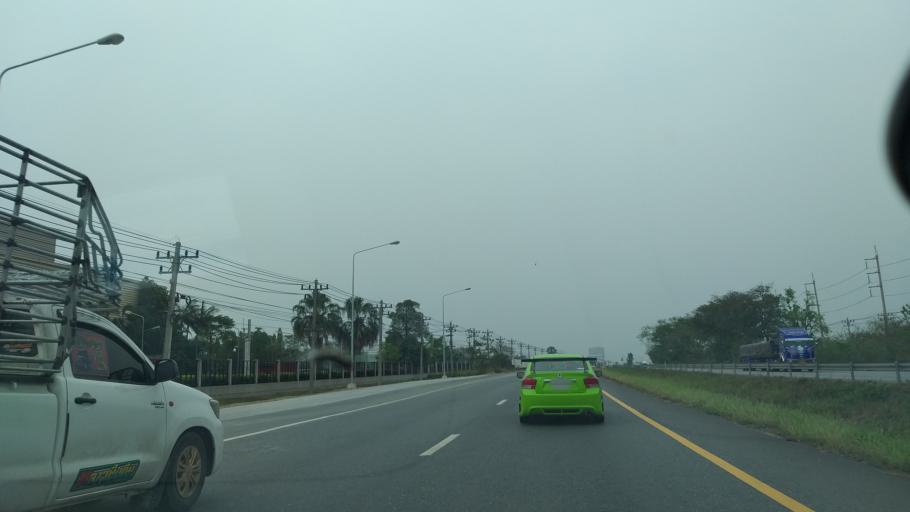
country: TH
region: Chon Buri
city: Ko Chan
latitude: 13.3490
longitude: 101.2708
